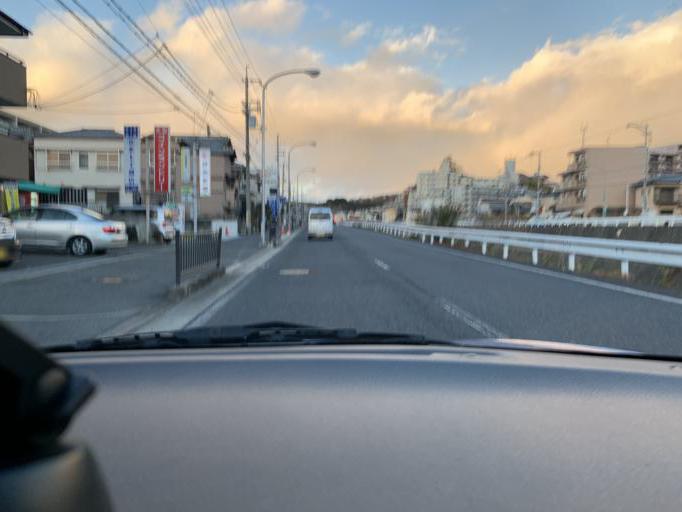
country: JP
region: Nara
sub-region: Ikoma-shi
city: Ikoma
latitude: 34.6990
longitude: 135.7322
